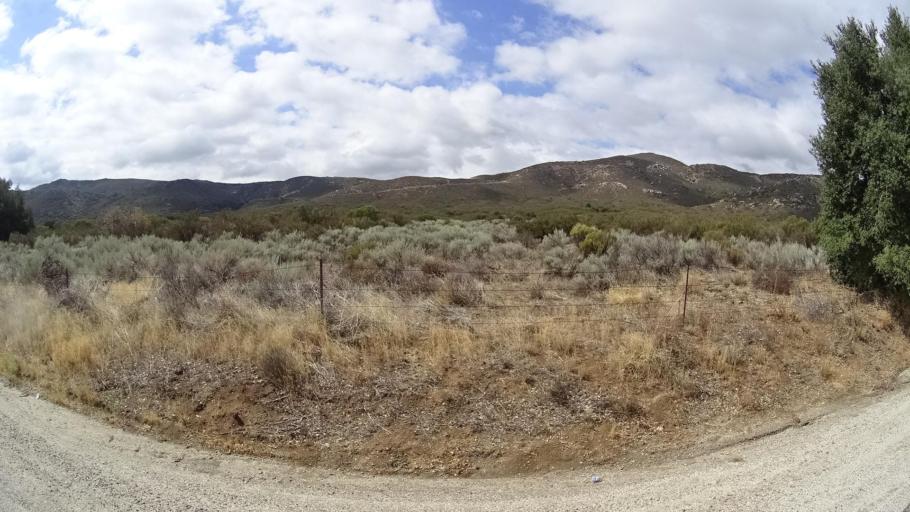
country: US
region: California
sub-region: San Diego County
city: Pine Valley
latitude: 32.7531
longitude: -116.4935
